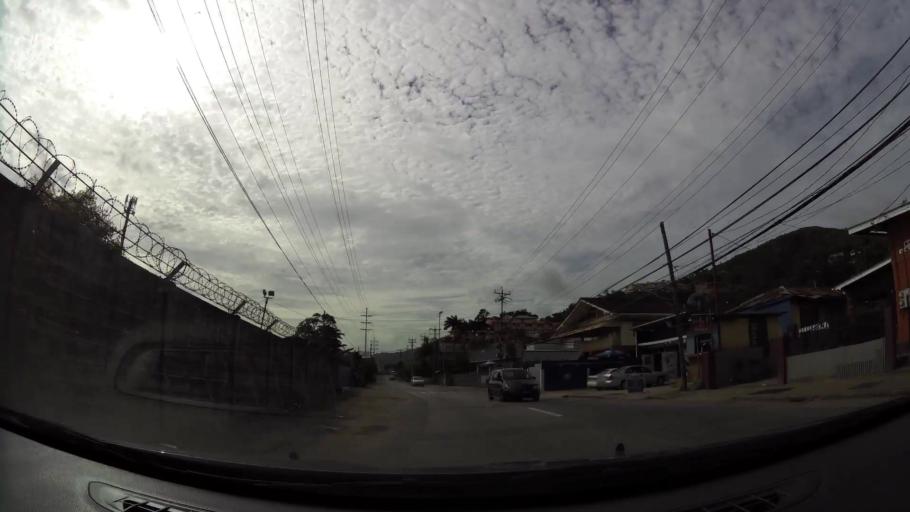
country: TT
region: City of Port of Spain
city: Mucurapo
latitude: 10.6821
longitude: -61.5802
